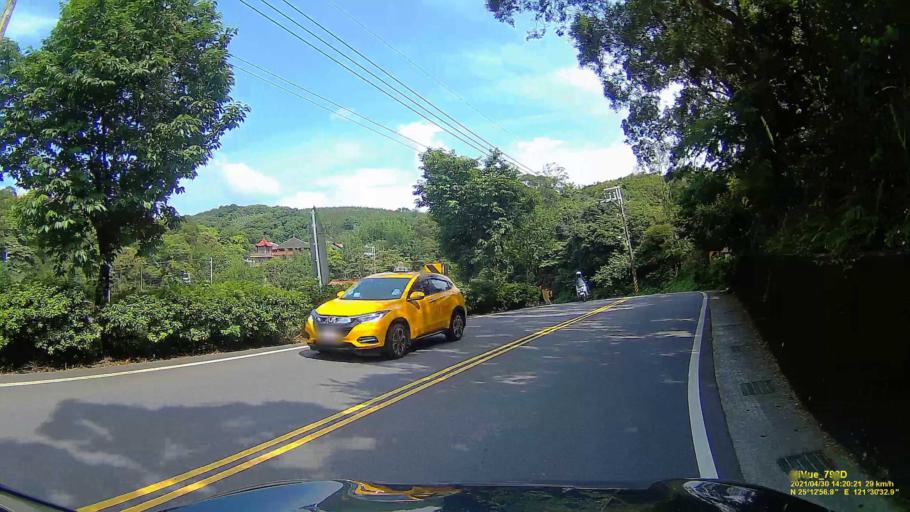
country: TW
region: Taipei
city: Taipei
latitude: 25.2158
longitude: 121.5092
